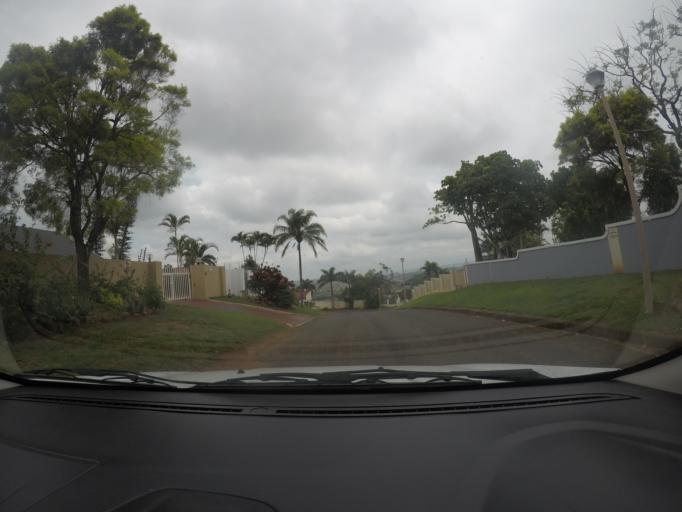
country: ZA
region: KwaZulu-Natal
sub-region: uThungulu District Municipality
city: Empangeni
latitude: -28.7550
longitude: 31.8870
